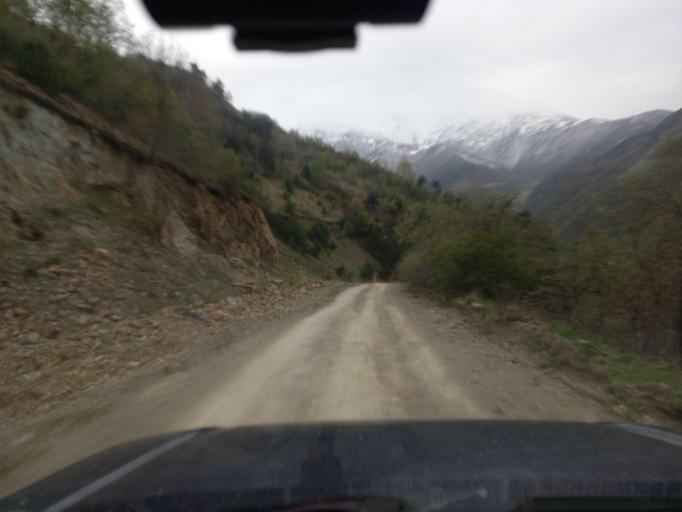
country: RU
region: North Ossetia
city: Mizur
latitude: 42.8540
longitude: 44.1647
